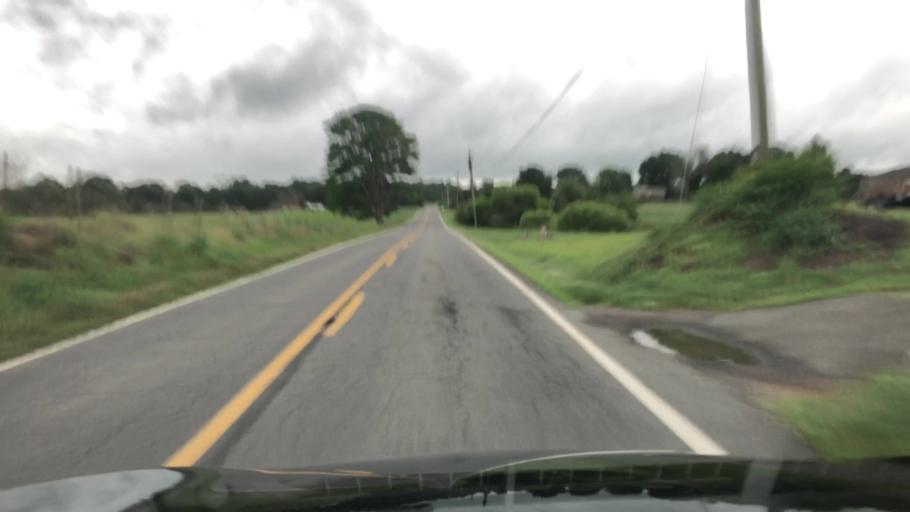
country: US
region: Virginia
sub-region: Prince William County
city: Nokesville
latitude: 38.5925
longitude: -77.6022
